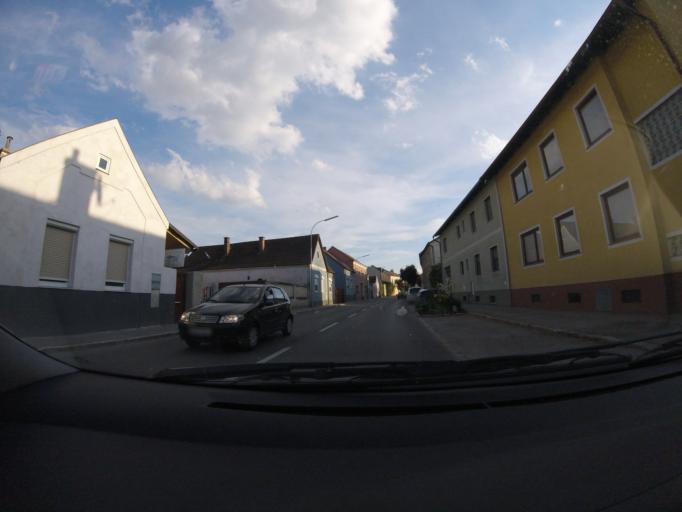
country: AT
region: Lower Austria
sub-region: Politischer Bezirk Wiener Neustadt
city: Zillingdorf
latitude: 47.8594
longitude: 16.3234
